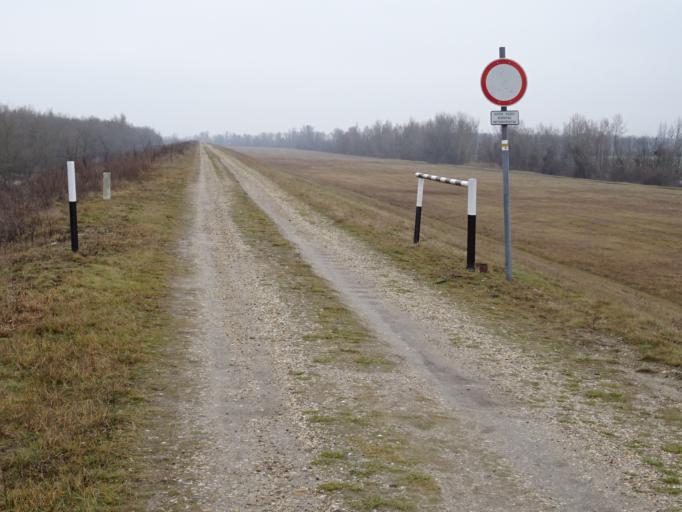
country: HU
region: Gyor-Moson-Sopron
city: Rajka
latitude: 47.9940
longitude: 17.2465
